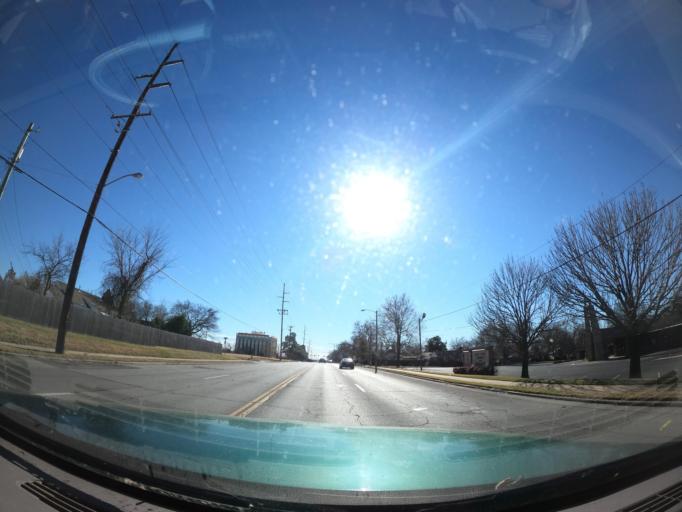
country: US
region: Oklahoma
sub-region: Tulsa County
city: Tulsa
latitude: 36.1306
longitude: -95.9404
